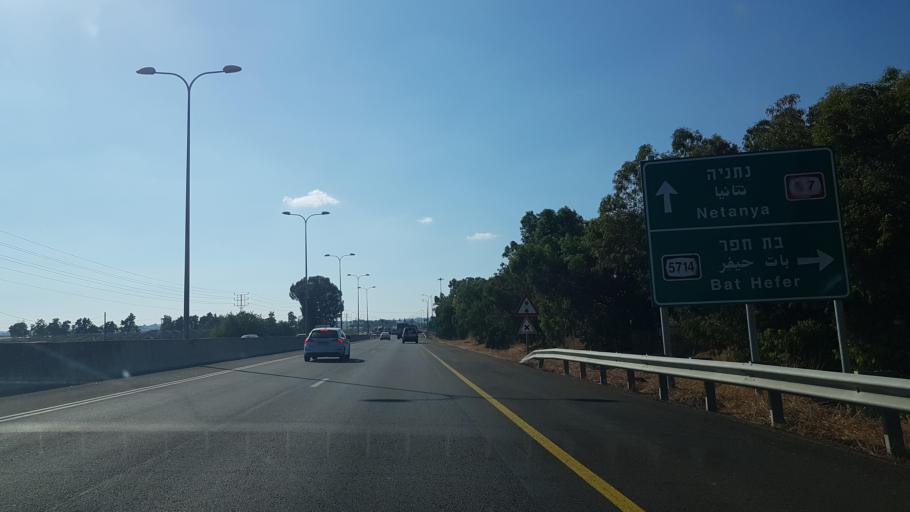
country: PS
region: West Bank
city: Tulkarm
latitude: 32.3120
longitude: 35.0031
